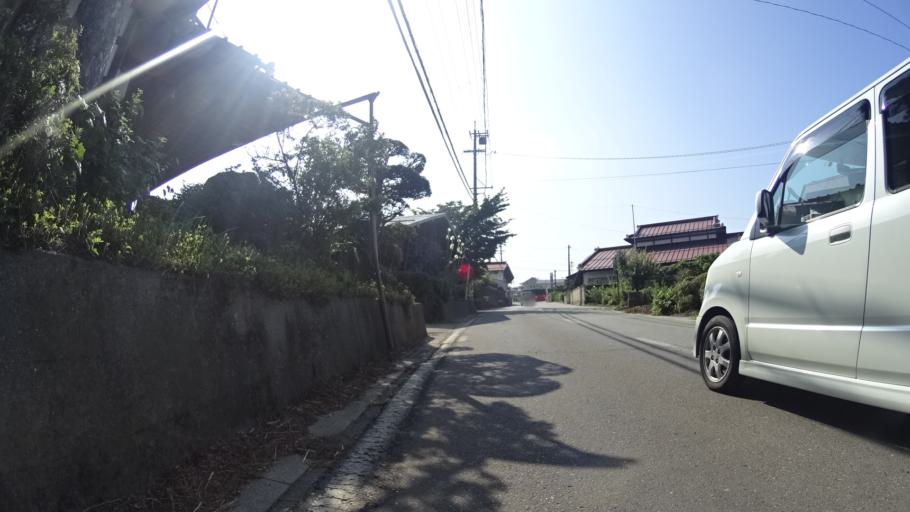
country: JP
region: Nagano
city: Chino
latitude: 35.9551
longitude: 138.2367
